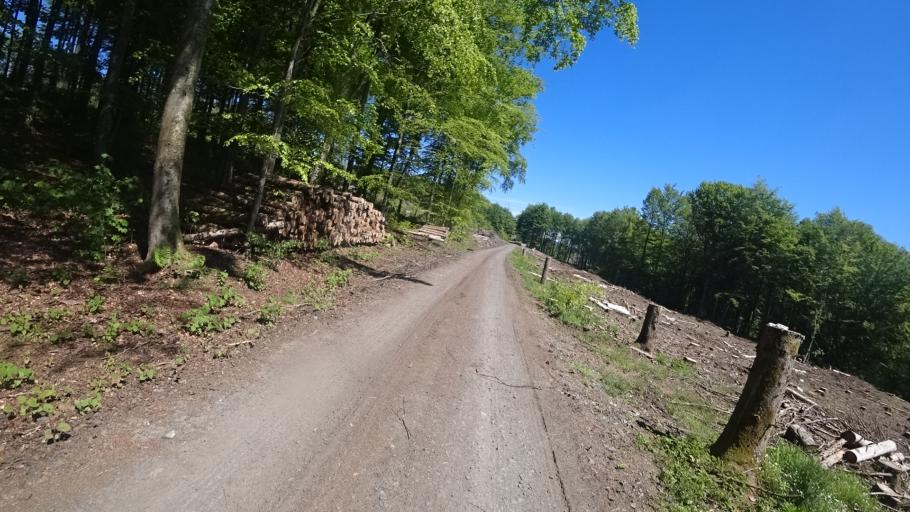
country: DE
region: Rheinland-Pfalz
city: Schutzbach
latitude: 50.7481
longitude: 7.8872
